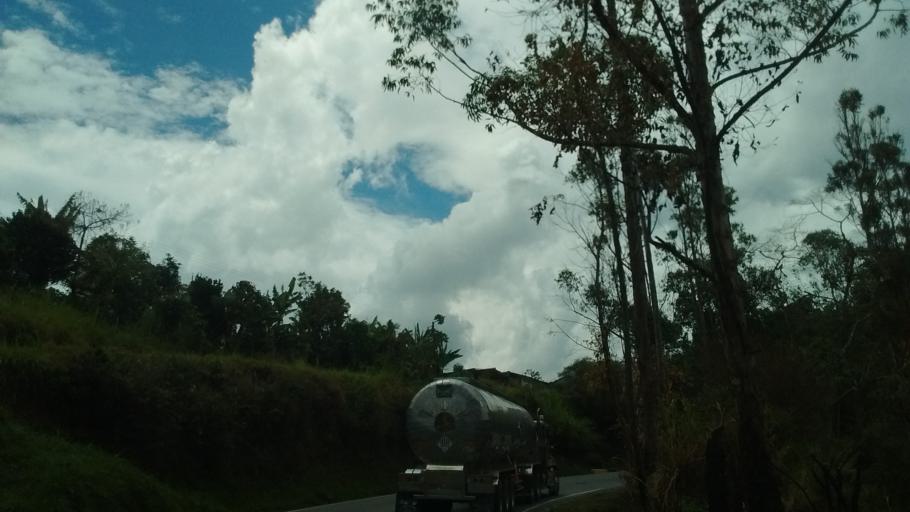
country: CO
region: Cauca
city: Rosas
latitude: 2.3215
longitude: -76.6890
